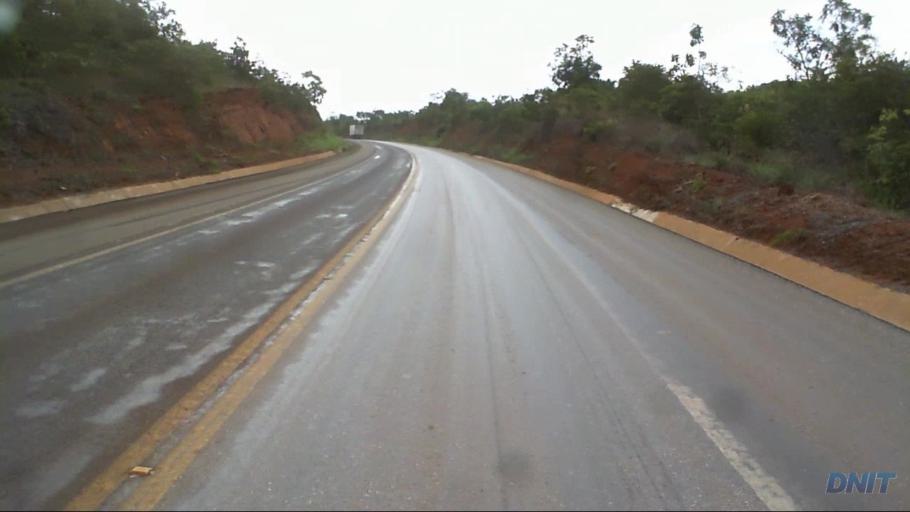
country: BR
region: Goias
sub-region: Barro Alto
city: Barro Alto
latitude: -14.9359
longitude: -48.9470
